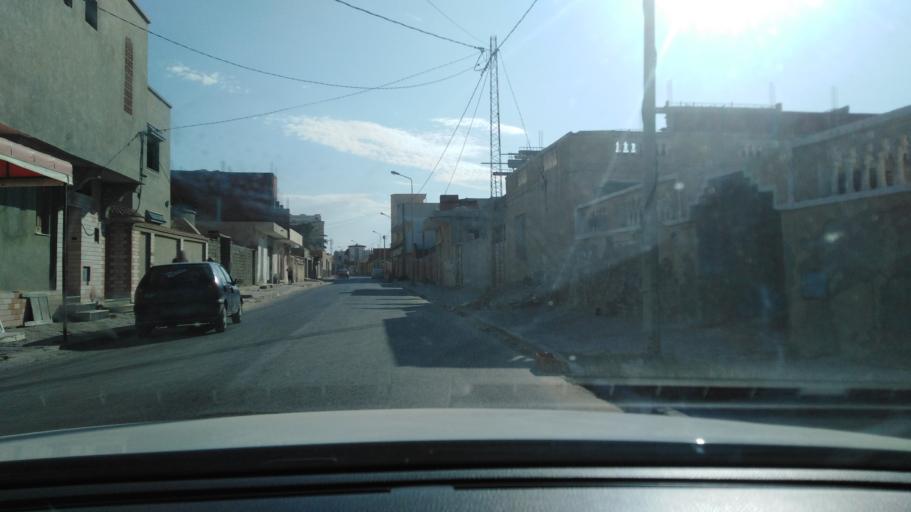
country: TN
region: Qabis
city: Gabes
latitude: 33.9407
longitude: 10.0727
